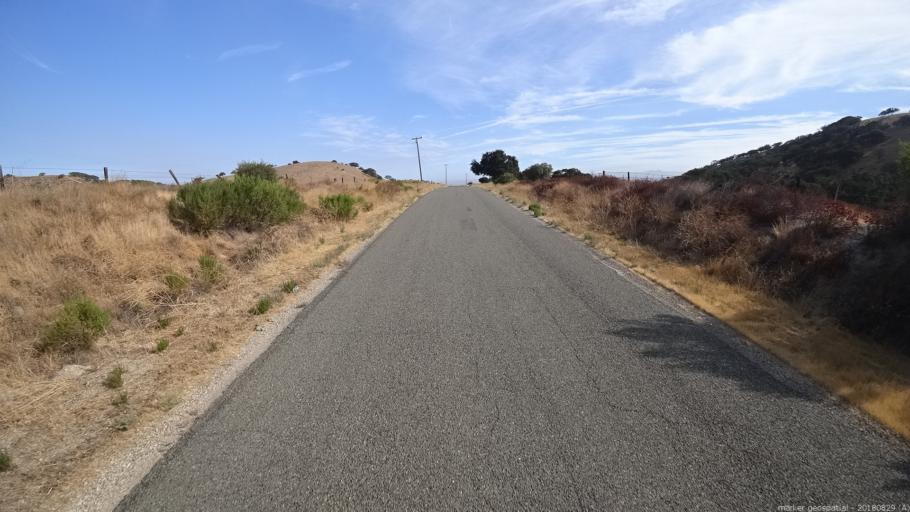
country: US
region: California
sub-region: Monterey County
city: King City
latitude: 36.0655
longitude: -121.0412
